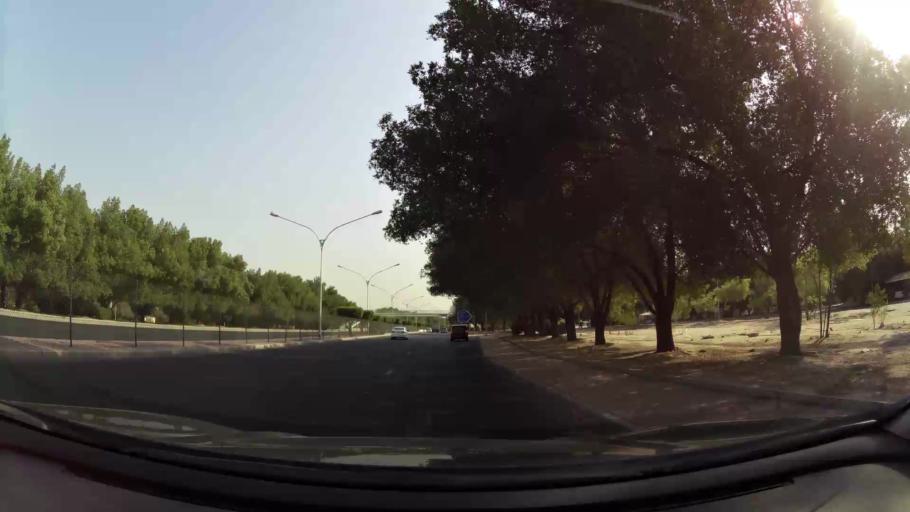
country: KW
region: Muhafazat Hawalli
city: Salwa
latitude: 29.2824
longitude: 48.0613
